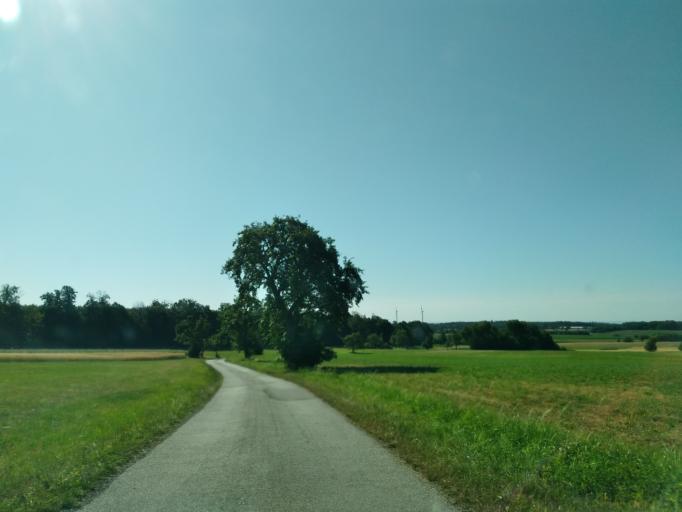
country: DE
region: Baden-Wuerttemberg
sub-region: Karlsruhe Region
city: Limbach
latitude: 49.4781
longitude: 9.2431
